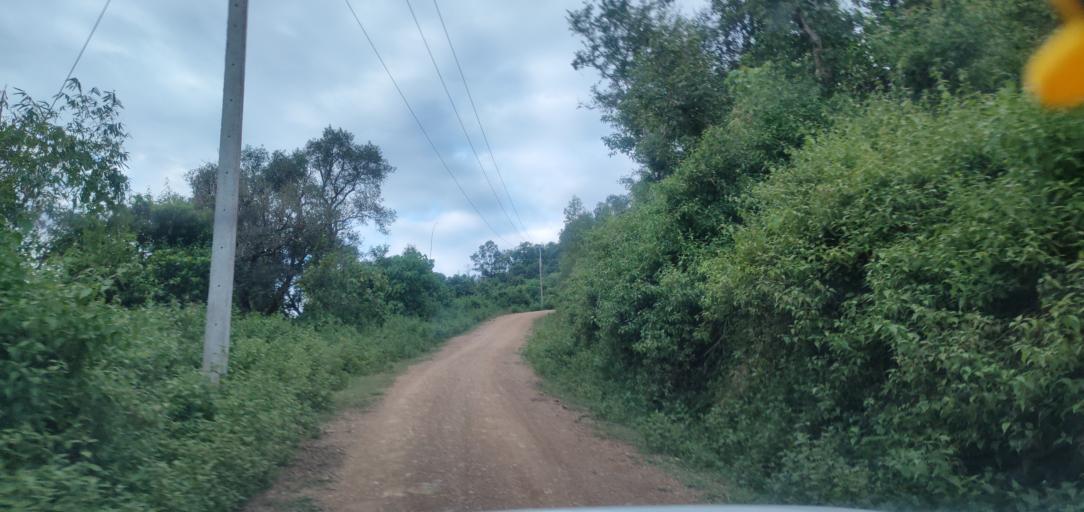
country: LA
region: Phongsali
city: Khoa
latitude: 21.1941
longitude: 102.2582
